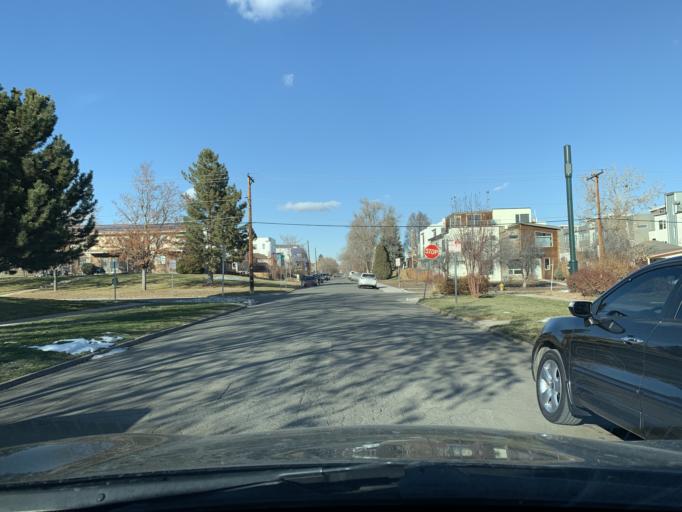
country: US
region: Colorado
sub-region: Jefferson County
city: Edgewater
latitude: 39.7448
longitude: -105.0284
